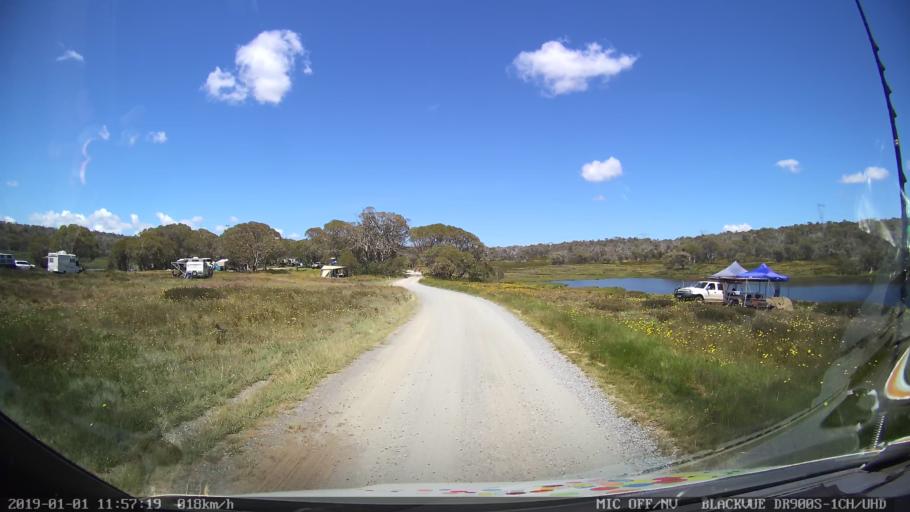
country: AU
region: New South Wales
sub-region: Snowy River
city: Jindabyne
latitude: -35.8874
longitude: 148.4493
